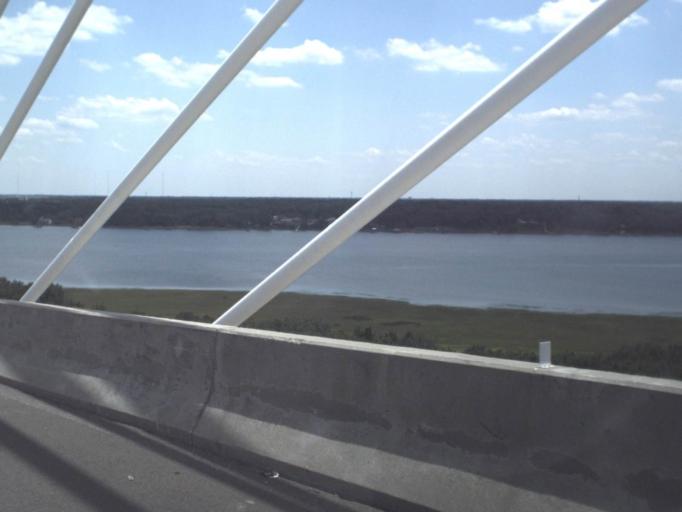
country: US
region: Florida
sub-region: Duval County
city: Jacksonville
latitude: 30.3822
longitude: -81.5561
